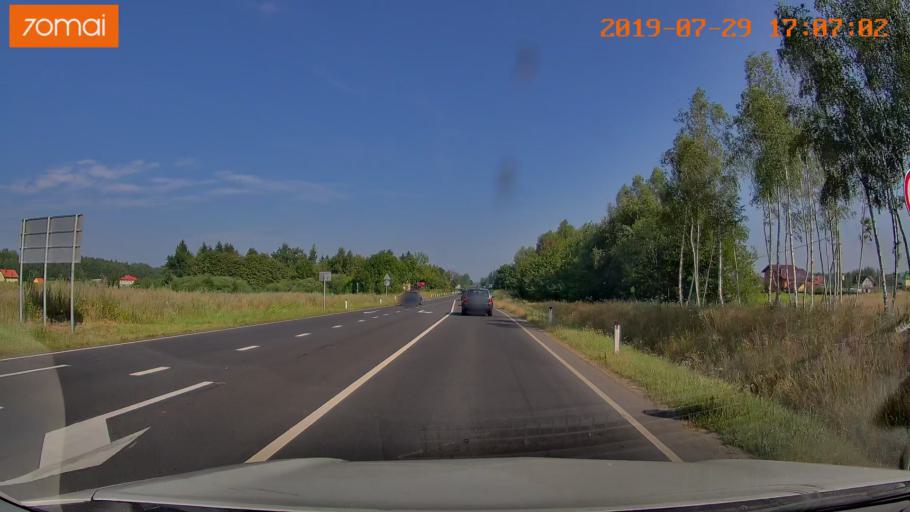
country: RU
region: Kaliningrad
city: Vzmorye
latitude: 54.8185
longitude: 20.3162
